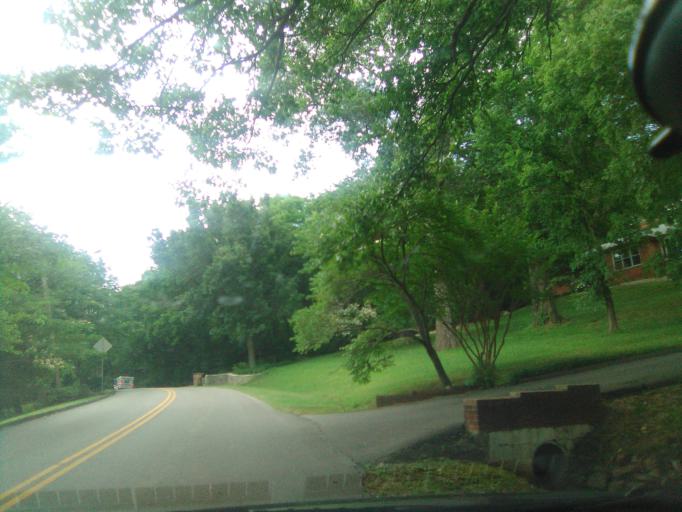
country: US
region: Tennessee
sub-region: Davidson County
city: Belle Meade
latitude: 36.1302
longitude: -86.8736
